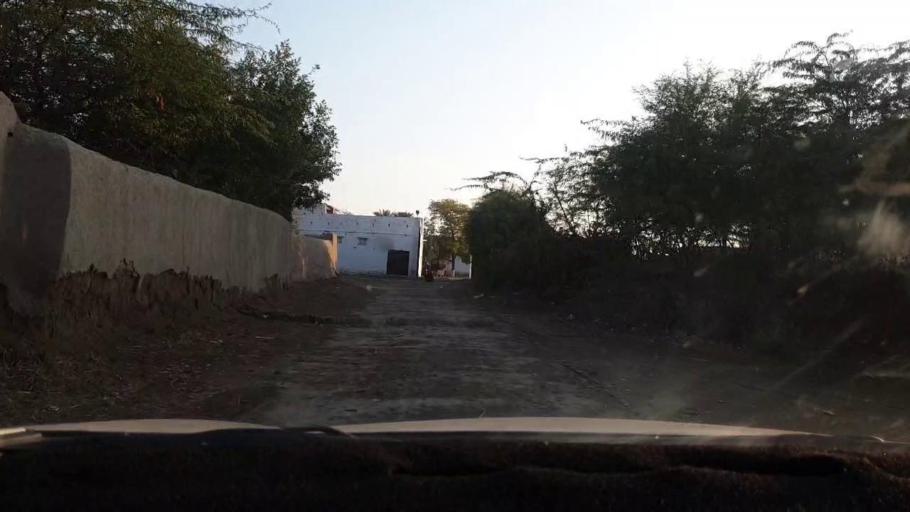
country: PK
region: Sindh
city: Berani
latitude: 25.7749
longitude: 68.7741
